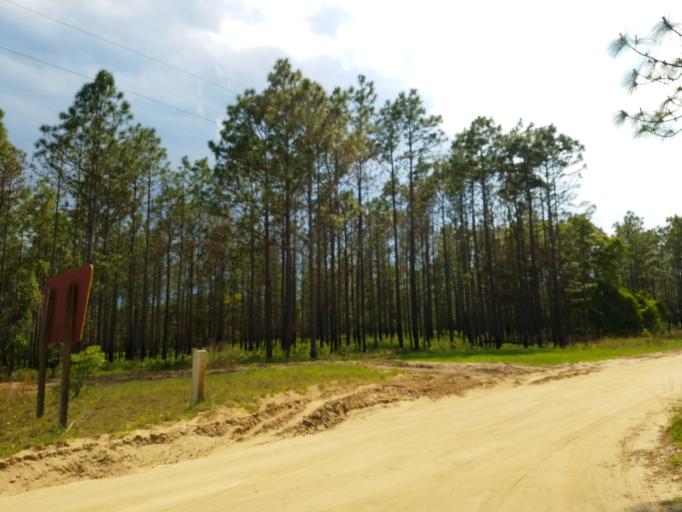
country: US
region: Florida
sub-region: Hernando County
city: Hill 'n Dale
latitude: 28.5575
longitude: -82.2679
